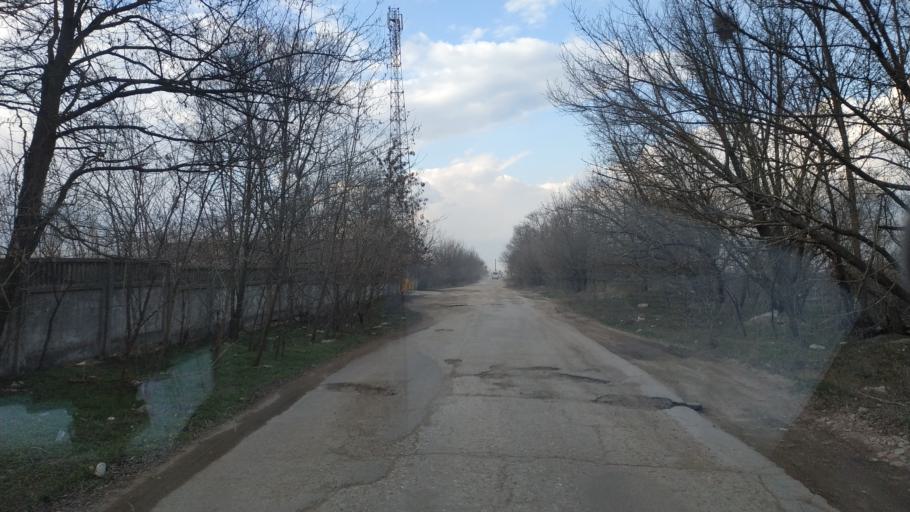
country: MD
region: Anenii Noi
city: Varnita
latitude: 46.8998
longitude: 29.4587
